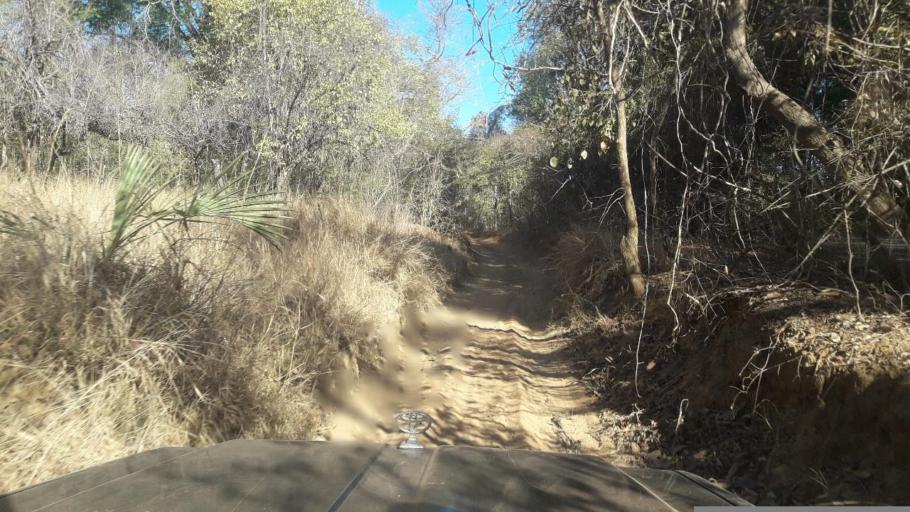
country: MG
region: Boeny
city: Sitampiky
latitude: -16.3963
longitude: 45.5948
